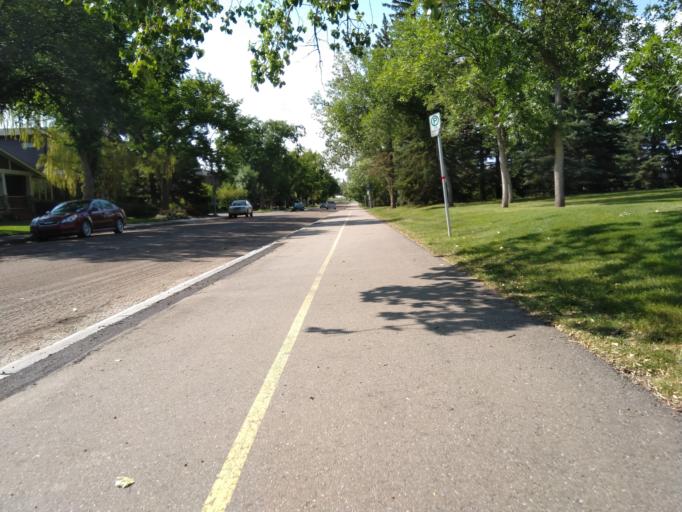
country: CA
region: Alberta
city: Calgary
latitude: 51.0798
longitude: -114.1118
